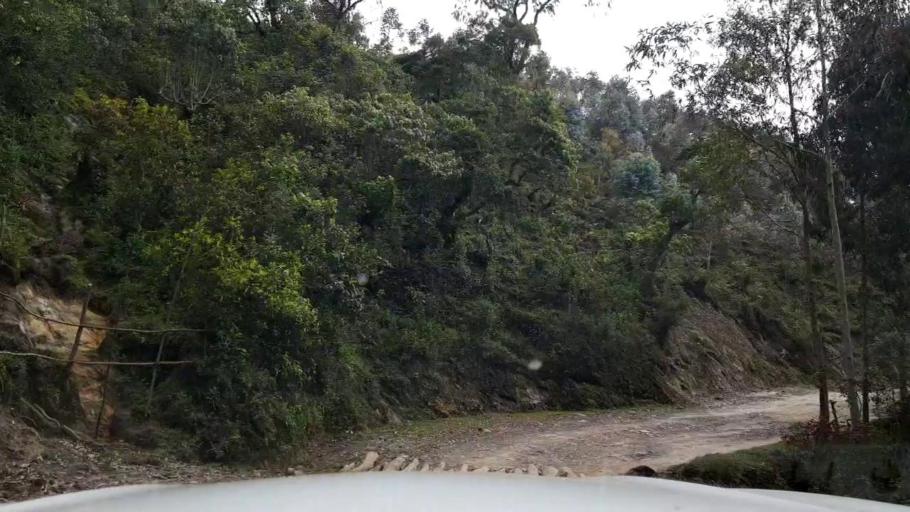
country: RW
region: Western Province
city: Kibuye
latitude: -1.9687
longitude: 29.4871
